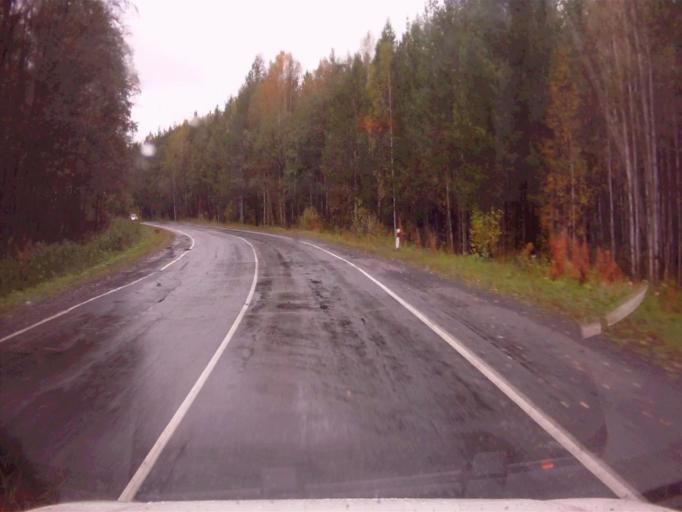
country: RU
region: Chelyabinsk
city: Verkhniy Ufaley
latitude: 55.9579
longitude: 60.3896
